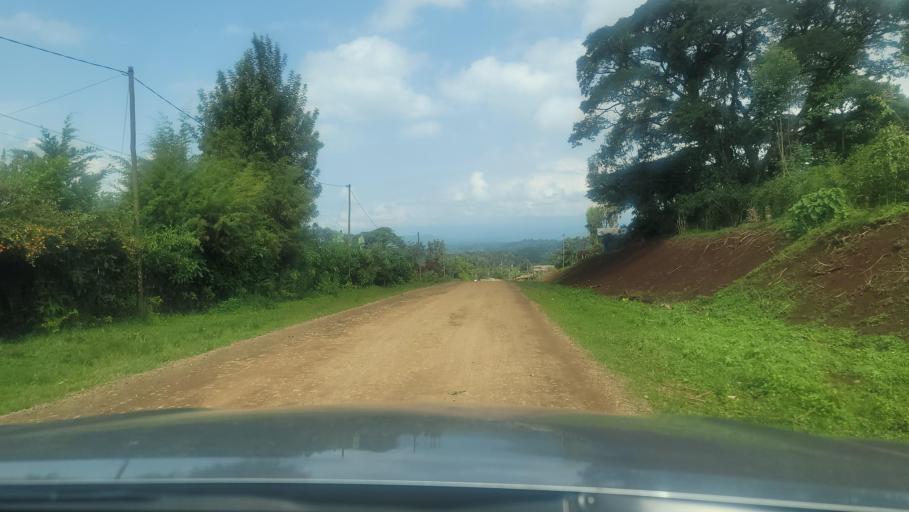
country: ET
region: Oromiya
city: Agaro
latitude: 7.7941
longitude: 36.4460
